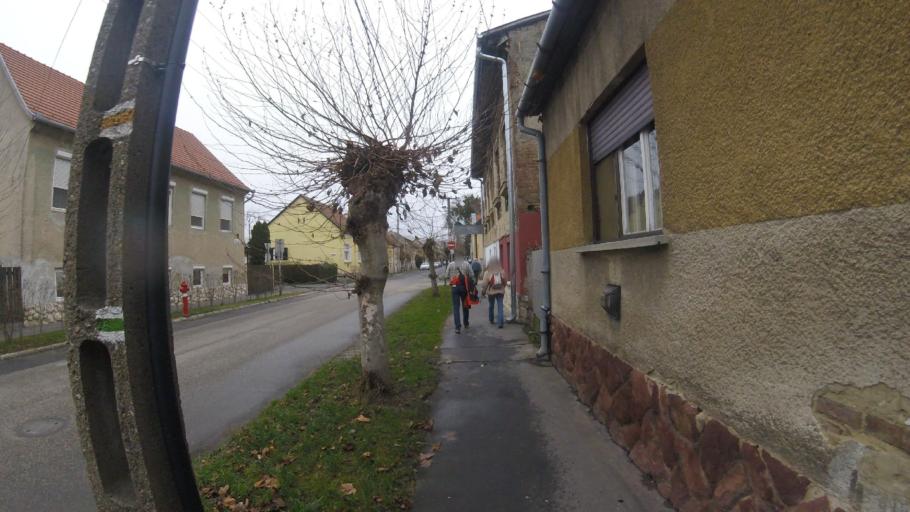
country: HU
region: Somogy
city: Kaposvar
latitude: 46.3522
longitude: 17.7875
